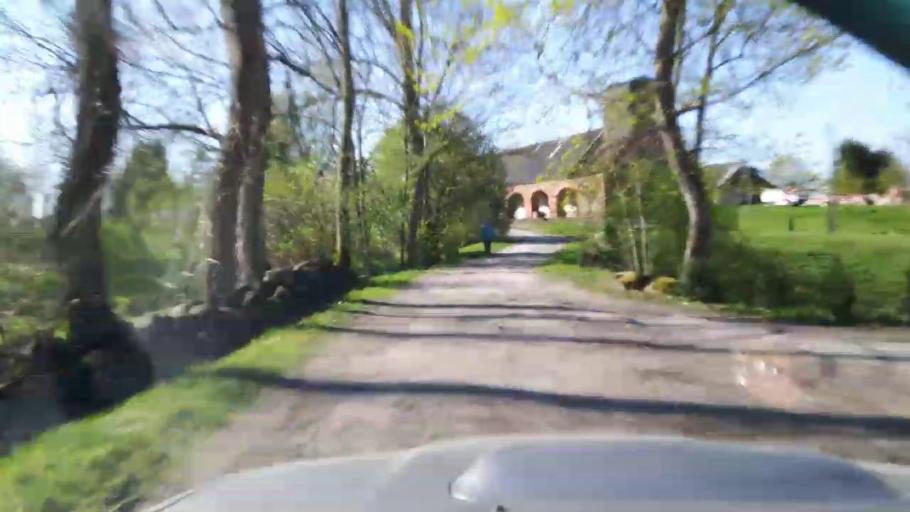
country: EE
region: Paernumaa
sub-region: Sindi linn
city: Sindi
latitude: 58.4483
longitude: 24.7641
